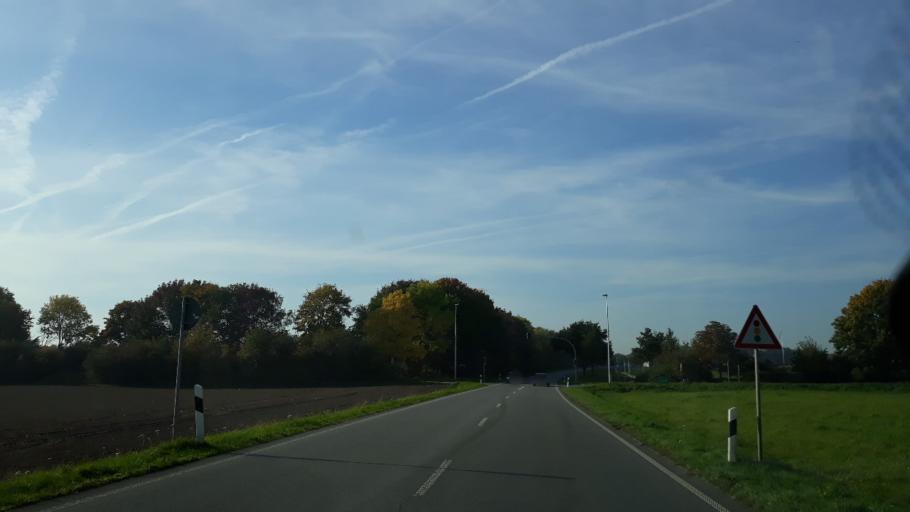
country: DE
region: Schleswig-Holstein
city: Schleswig
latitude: 54.5314
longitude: 9.5688
